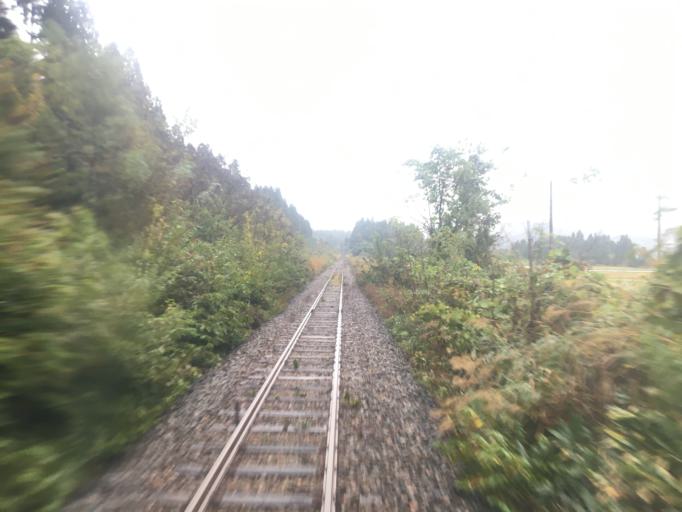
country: JP
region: Yamagata
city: Shinjo
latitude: 38.7054
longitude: 140.3395
